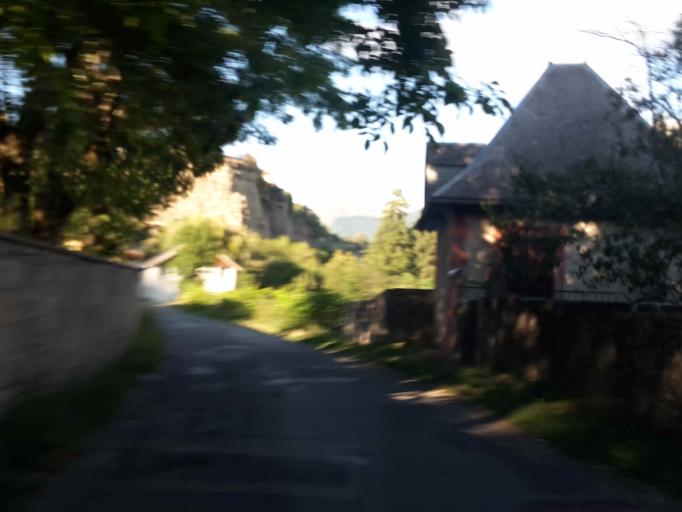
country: FR
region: Provence-Alpes-Cote d'Azur
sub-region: Departement des Hautes-Alpes
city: Embrun
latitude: 44.5588
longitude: 6.4897
